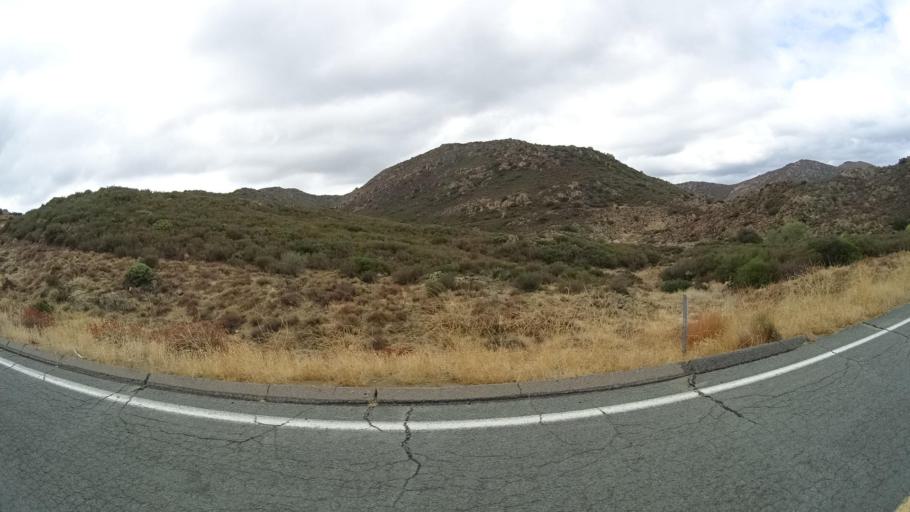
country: US
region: California
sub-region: San Diego County
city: Pine Valley
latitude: 32.7503
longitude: -116.4513
